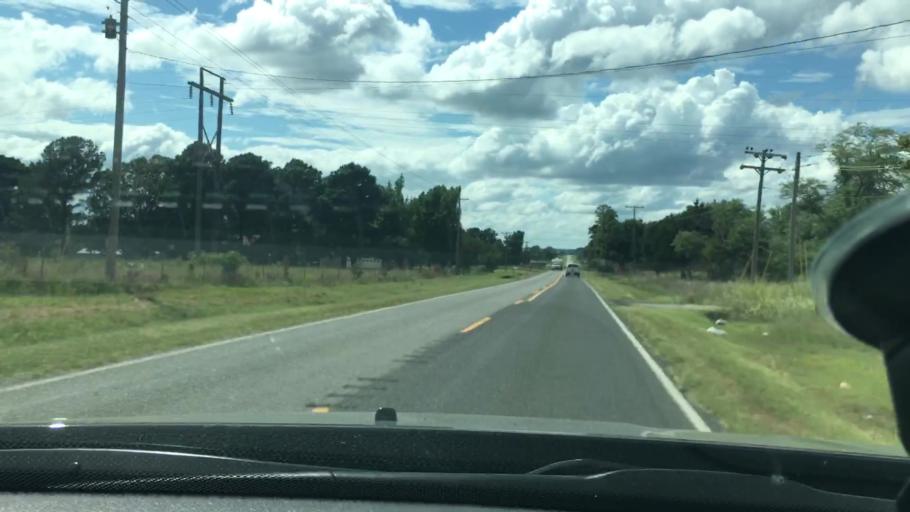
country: US
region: Oklahoma
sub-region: Sequoyah County
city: Vian
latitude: 35.6097
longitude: -94.9701
